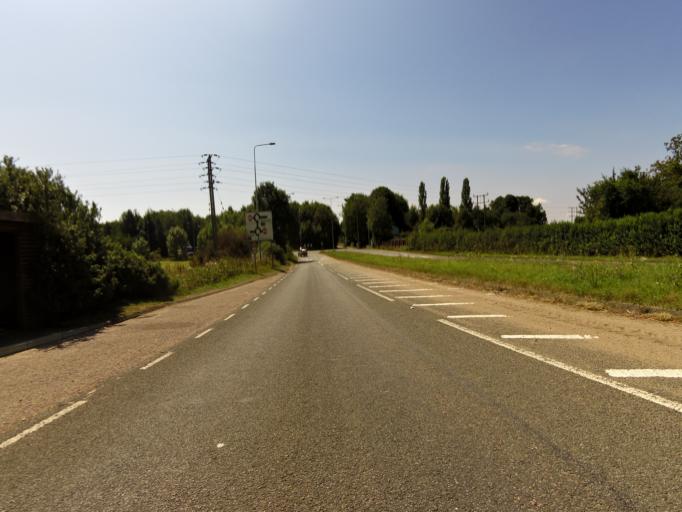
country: GB
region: England
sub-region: Suffolk
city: Capel Saint Mary
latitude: 52.0163
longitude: 1.0697
